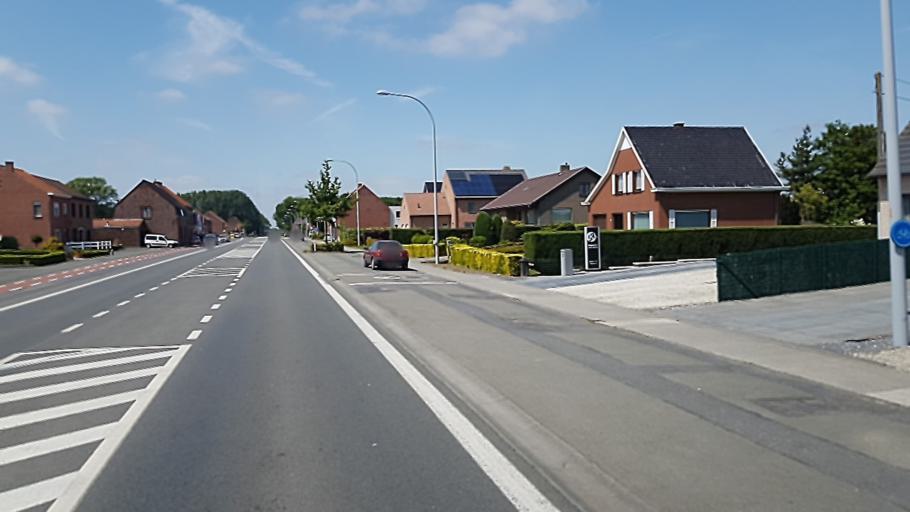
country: BE
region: Flanders
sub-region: Provincie West-Vlaanderen
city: Zonnebeke
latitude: 50.8377
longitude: 2.9812
